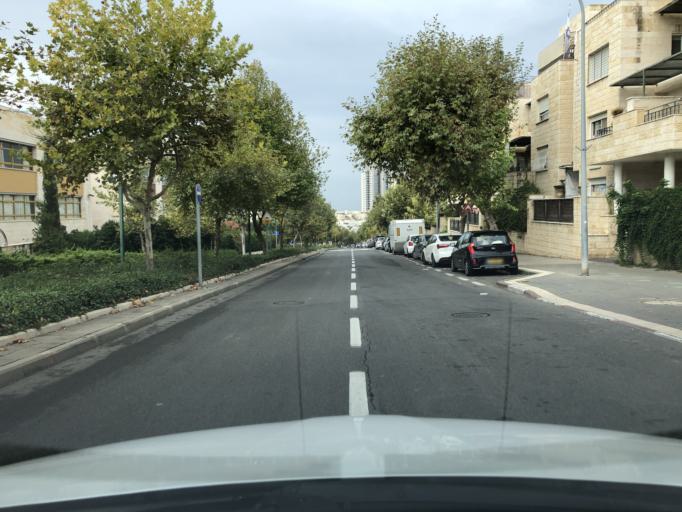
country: IL
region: Central District
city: Modiin
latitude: 31.9132
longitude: 35.0098
